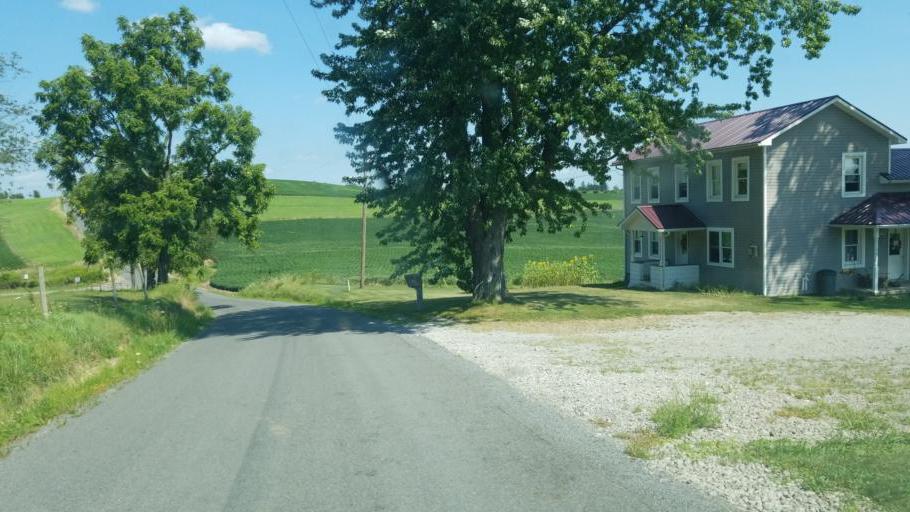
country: US
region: Pennsylvania
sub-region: Clarion County
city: Knox
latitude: 41.0942
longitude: -79.5209
